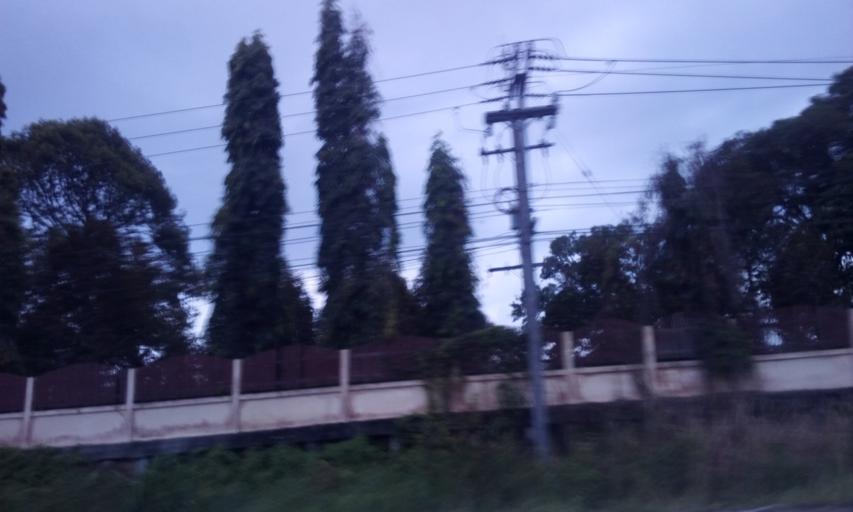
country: TH
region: Chanthaburi
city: Khlung
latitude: 12.4533
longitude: 102.2817
